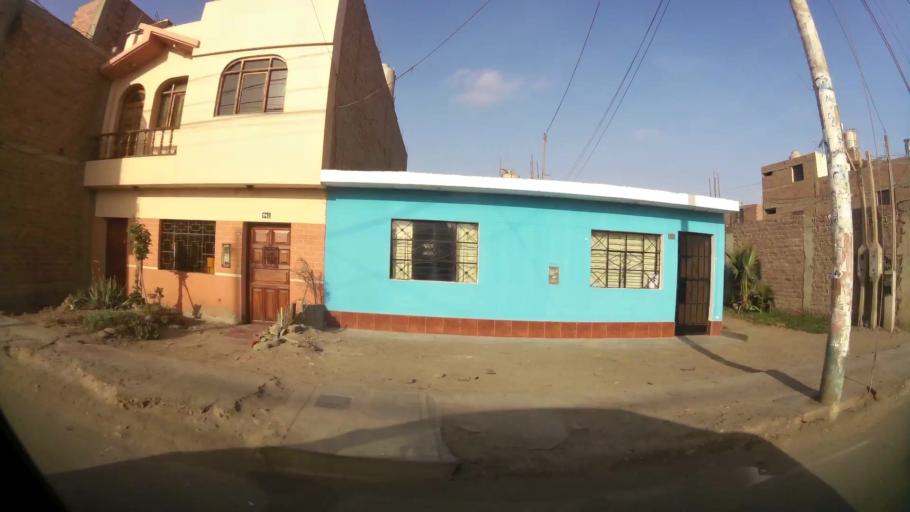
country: PE
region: Lima
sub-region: Huaura
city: Huacho
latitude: -11.1114
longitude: -77.6054
